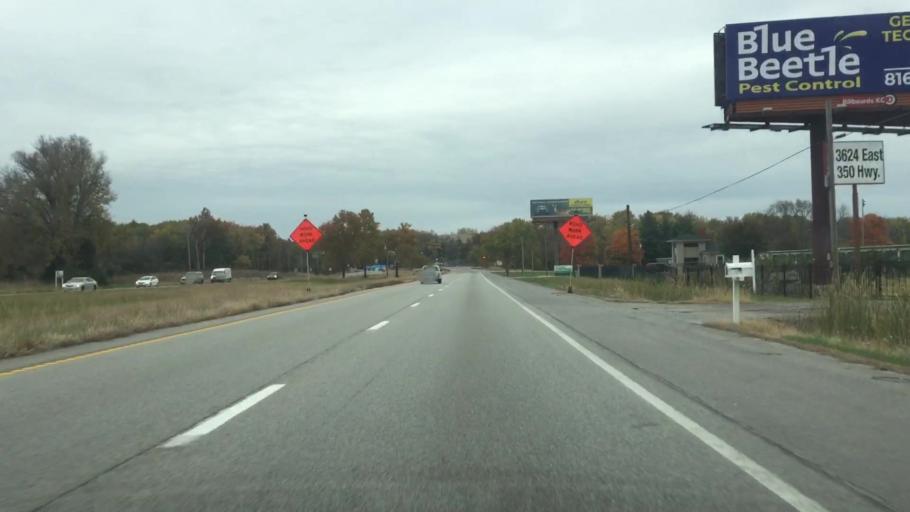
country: US
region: Missouri
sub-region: Jackson County
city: Raytown
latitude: 38.9612
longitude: -94.4241
